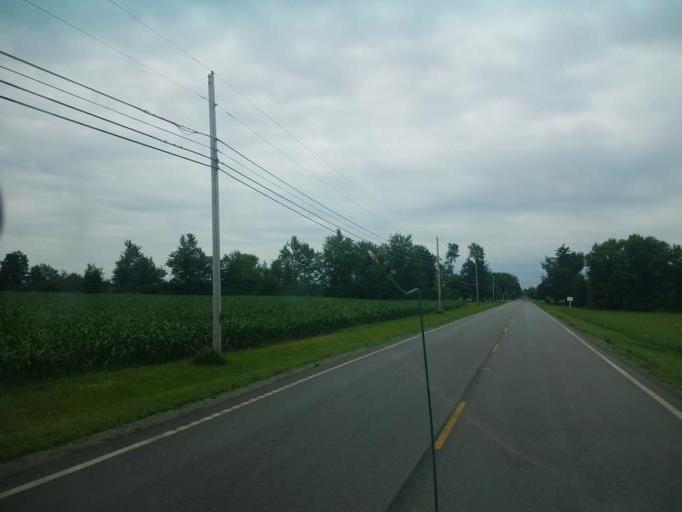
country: US
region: Ohio
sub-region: Hardin County
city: Ada
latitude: 40.7889
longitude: -83.8232
